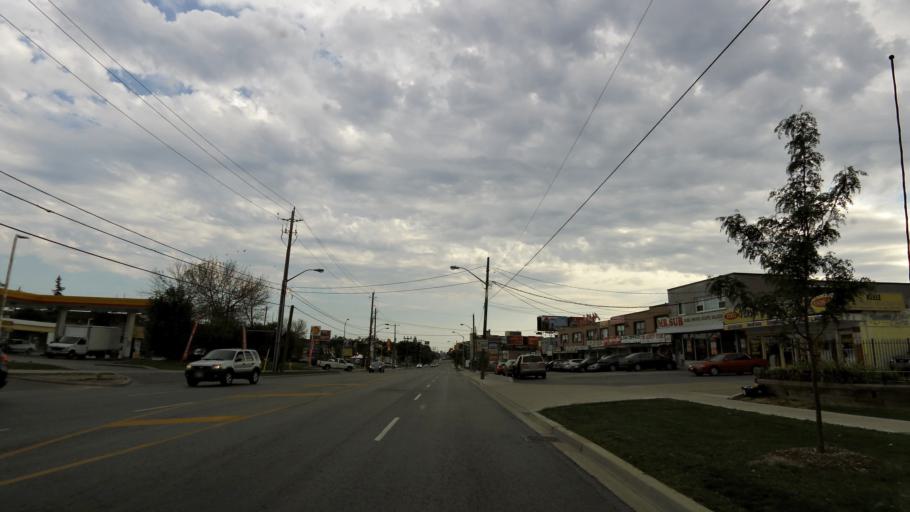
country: CA
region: Ontario
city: Toronto
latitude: 43.7039
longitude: -79.4770
